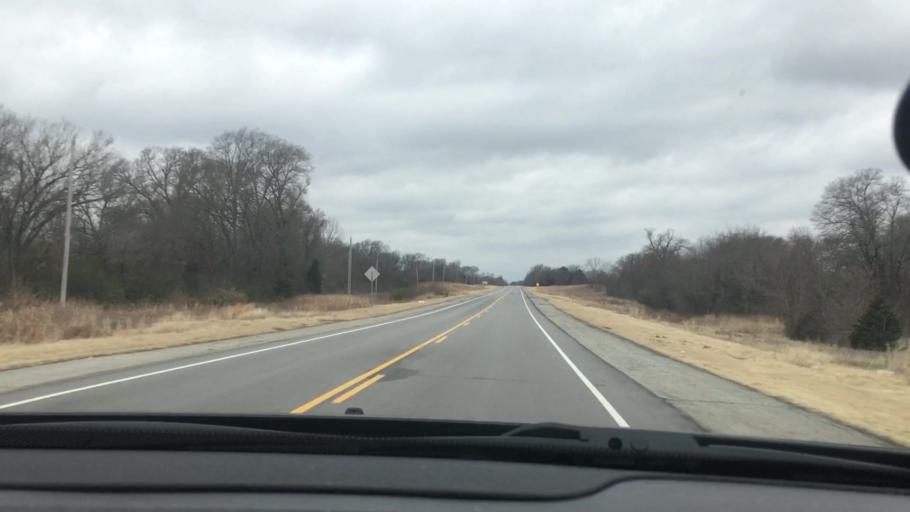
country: US
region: Oklahoma
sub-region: Atoka County
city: Atoka
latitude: 34.3749
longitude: -96.1555
